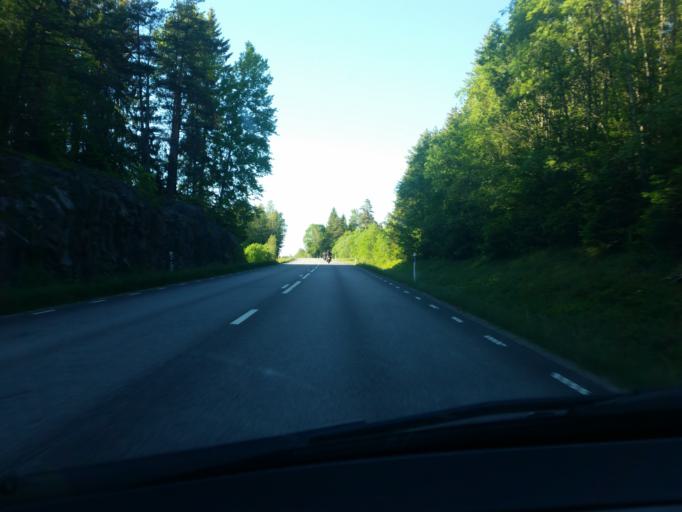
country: SE
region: Vaestra Goetaland
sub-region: Fargelanda Kommun
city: Faergelanda
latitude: 58.5327
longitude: 11.9826
